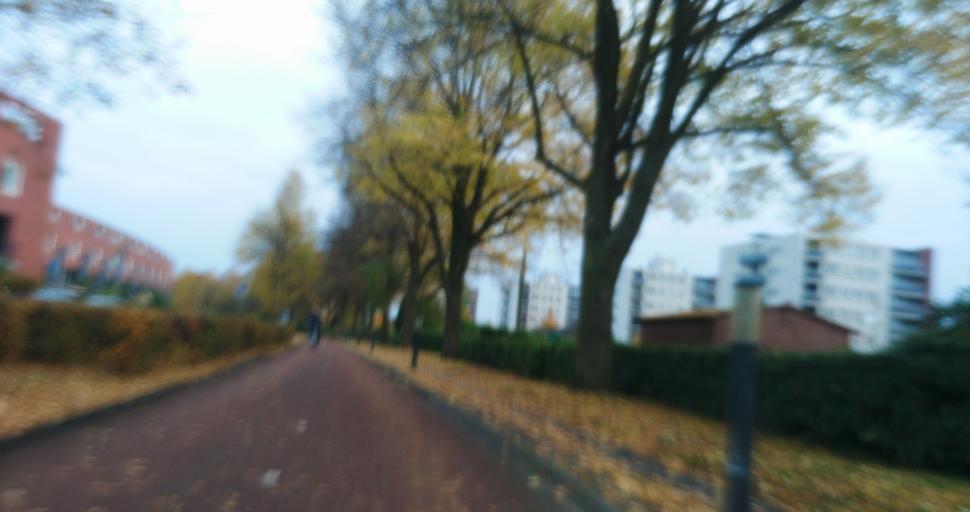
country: NL
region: Groningen
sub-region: Gemeente Groningen
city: Groningen
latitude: 53.2207
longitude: 6.5434
